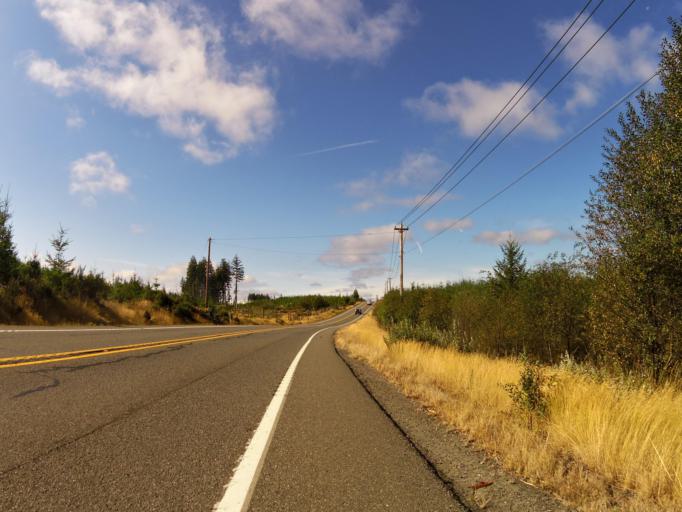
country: US
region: Washington
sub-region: Mason County
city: Allyn
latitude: 47.3279
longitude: -122.8889
